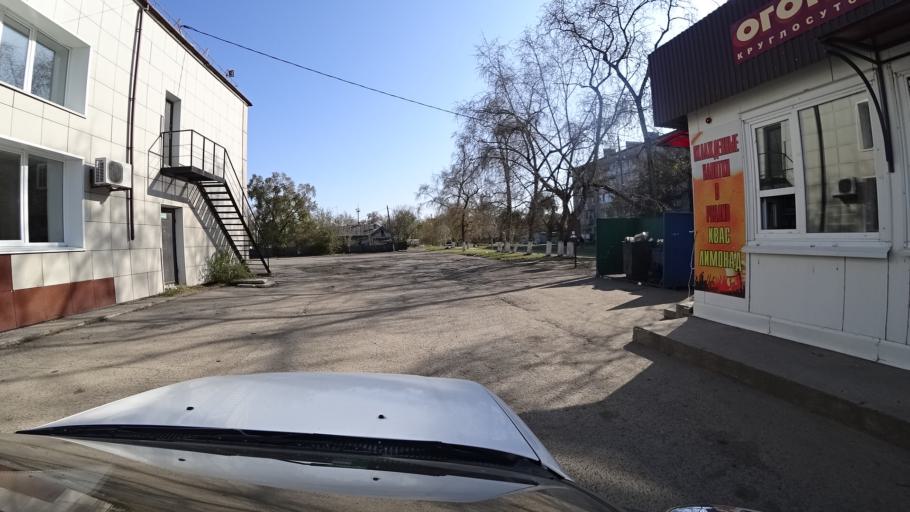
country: RU
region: Primorskiy
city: Dal'nerechensk
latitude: 45.9348
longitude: 133.7251
